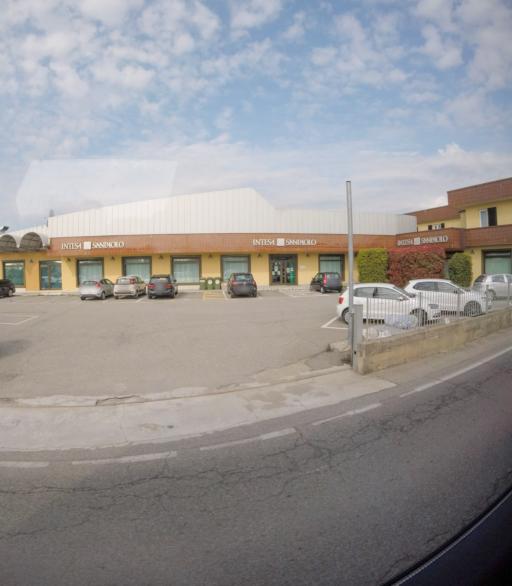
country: IT
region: Piedmont
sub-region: Provincia di Novara
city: Briga Novarese
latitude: 45.7270
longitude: 8.4449
